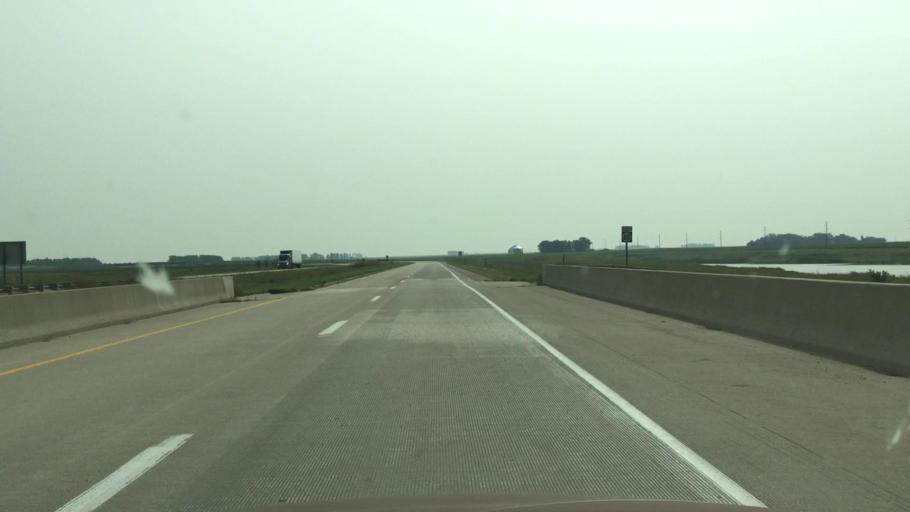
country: US
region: Iowa
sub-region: Osceola County
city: Sibley
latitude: 43.3843
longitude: -95.7370
